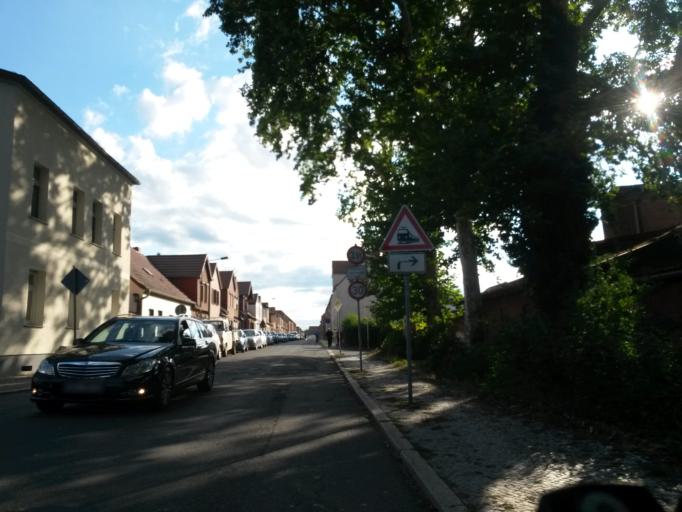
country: DE
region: Saxony-Anhalt
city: Tangermunde
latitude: 52.5450
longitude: 11.9695
